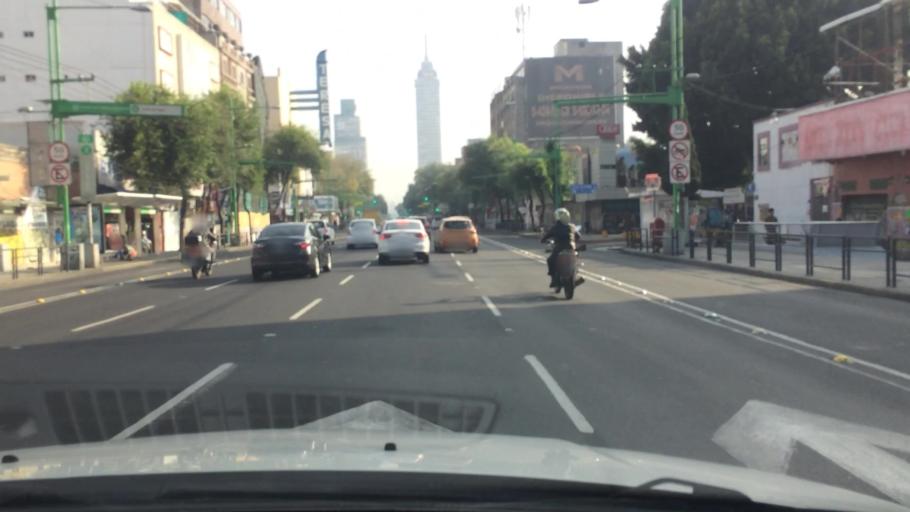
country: MX
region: Mexico City
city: Mexico City
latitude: 19.4270
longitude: -99.1420
